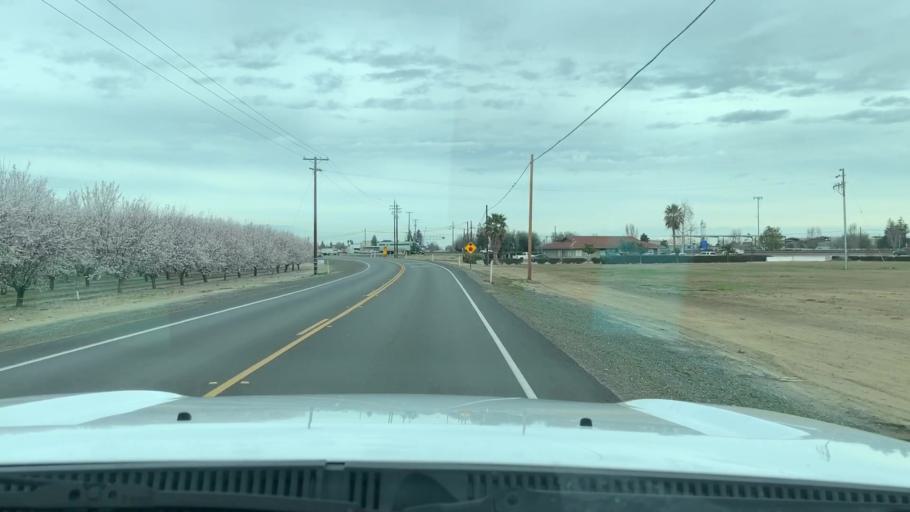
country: US
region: California
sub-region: Kern County
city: Shafter
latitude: 35.4898
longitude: -119.2607
